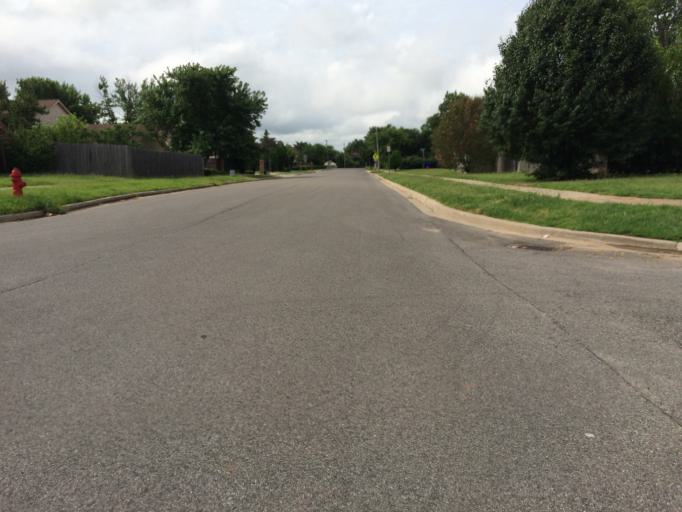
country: US
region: Oklahoma
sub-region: Cleveland County
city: Hall Park
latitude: 35.2205
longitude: -97.4134
